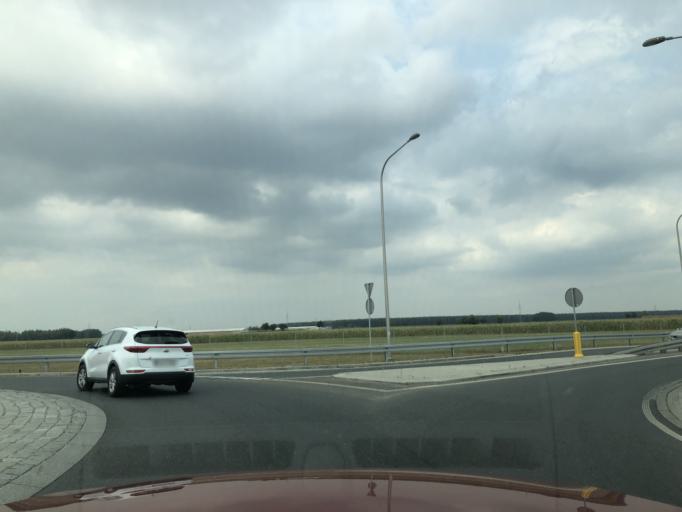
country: PL
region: Greater Poland Voivodeship
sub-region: Powiat leszczynski
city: Swieciechowa
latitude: 51.8615
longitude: 16.5135
